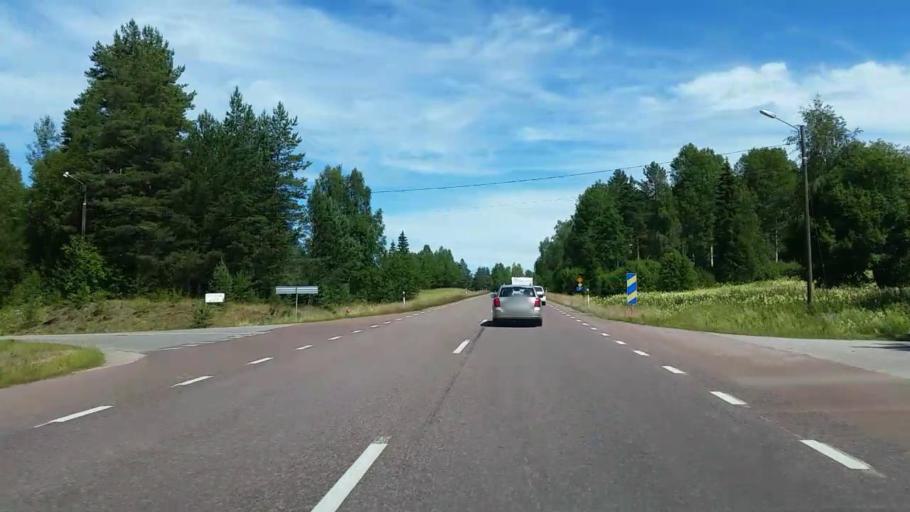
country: SE
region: Dalarna
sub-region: Rattviks Kommun
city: Raettvik
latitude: 60.9249
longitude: 15.2163
